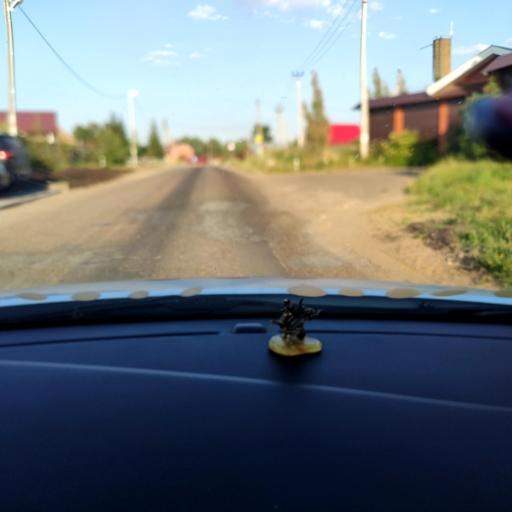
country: RU
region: Tatarstan
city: Pestretsy
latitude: 55.6160
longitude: 49.4897
